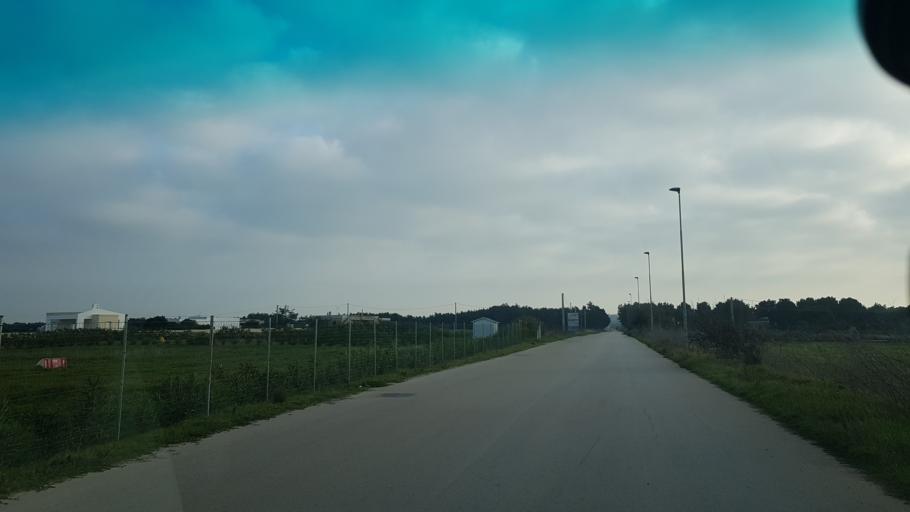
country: IT
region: Apulia
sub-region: Provincia di Brindisi
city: Carovigno
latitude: 40.7439
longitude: 17.7295
